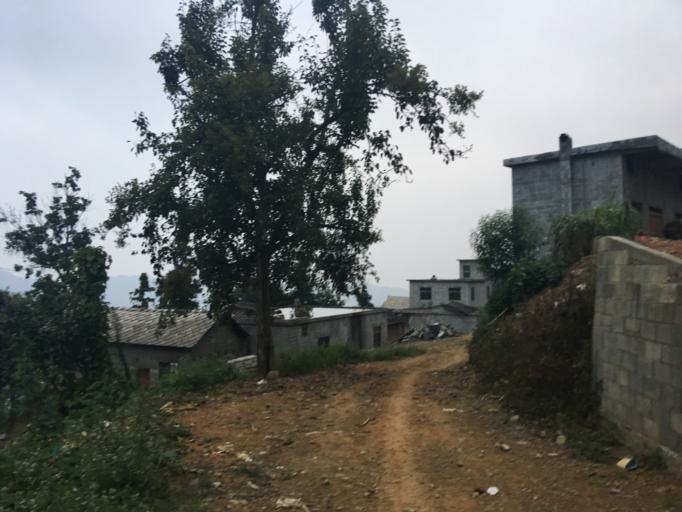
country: CN
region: Guangxi Zhuangzu Zizhiqu
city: Xinzhou
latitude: 24.9022
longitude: 105.5779
